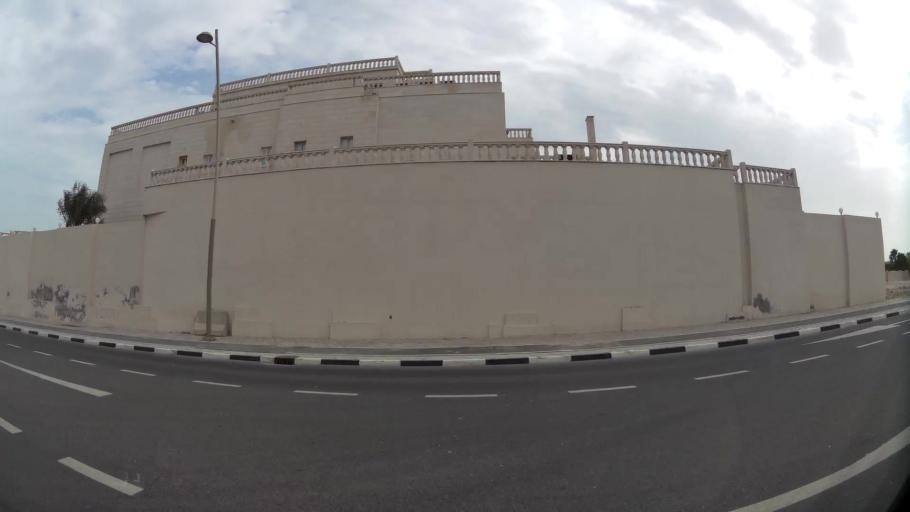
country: QA
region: Baladiyat ad Dawhah
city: Doha
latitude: 25.3383
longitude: 51.4898
